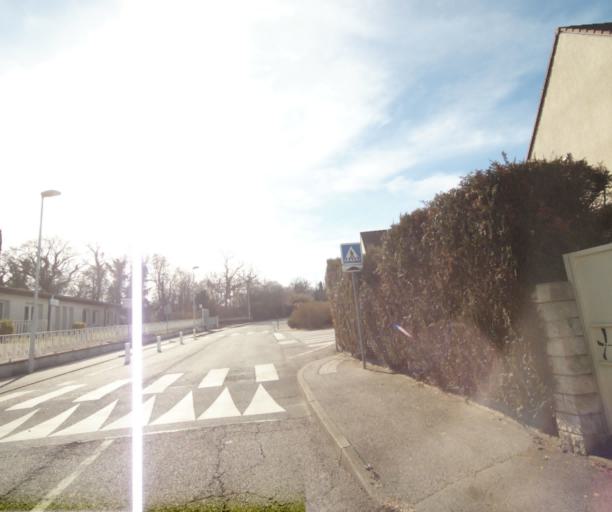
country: FR
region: Lorraine
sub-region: Departement de Meurthe-et-Moselle
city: Villers-les-Nancy
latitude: 48.6525
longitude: 6.1606
